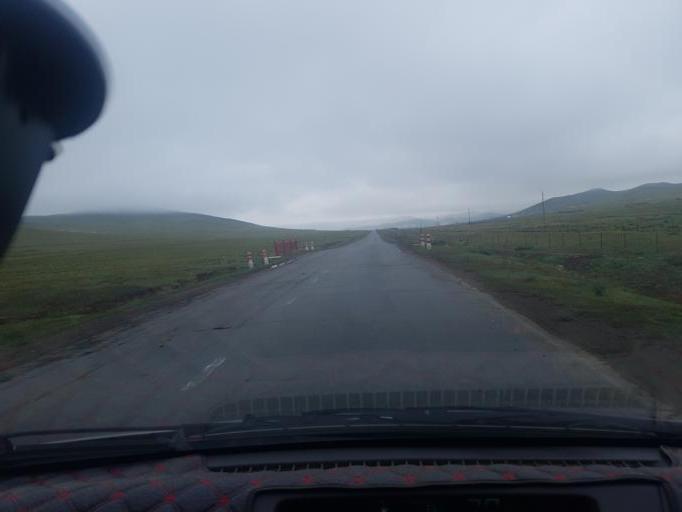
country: MN
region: Ulaanbaatar
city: Ulaanbaatar
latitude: 47.9808
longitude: 106.5706
